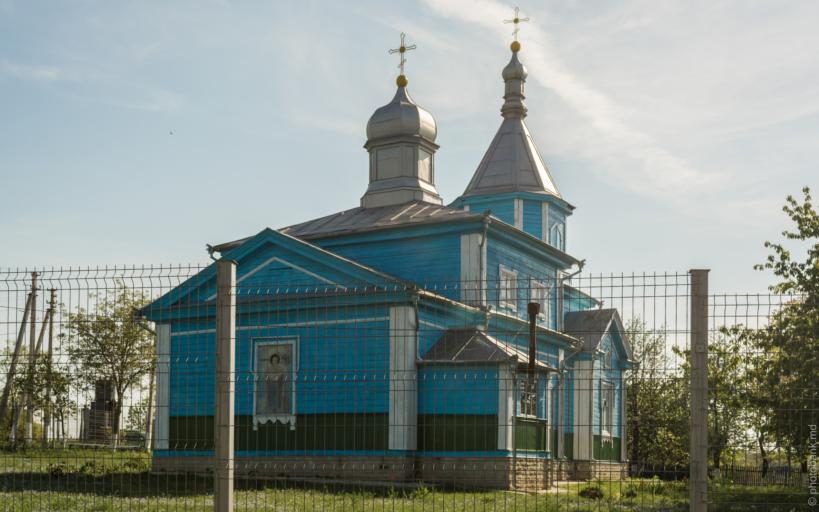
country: MD
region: Balti
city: Balti
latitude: 47.7075
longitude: 27.8698
